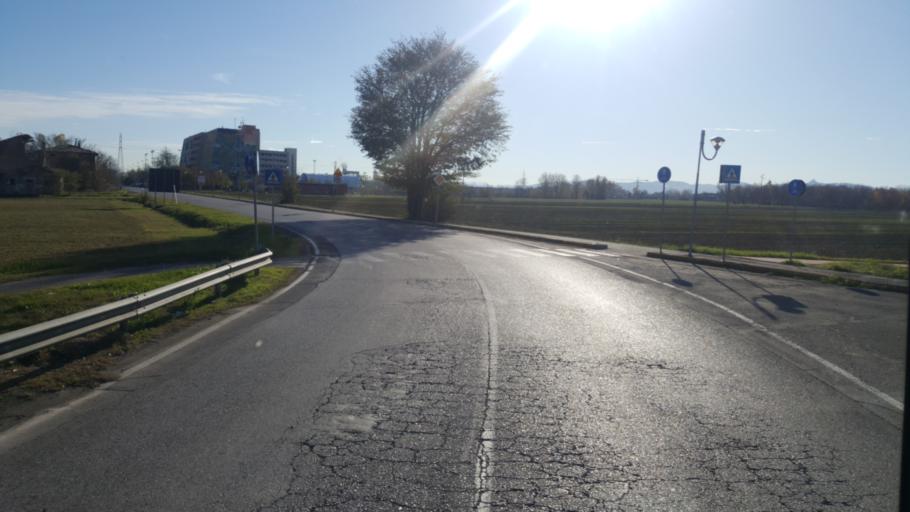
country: IT
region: Emilia-Romagna
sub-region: Provincia di Bologna
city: Calderara di Reno
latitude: 44.5563
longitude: 11.2771
